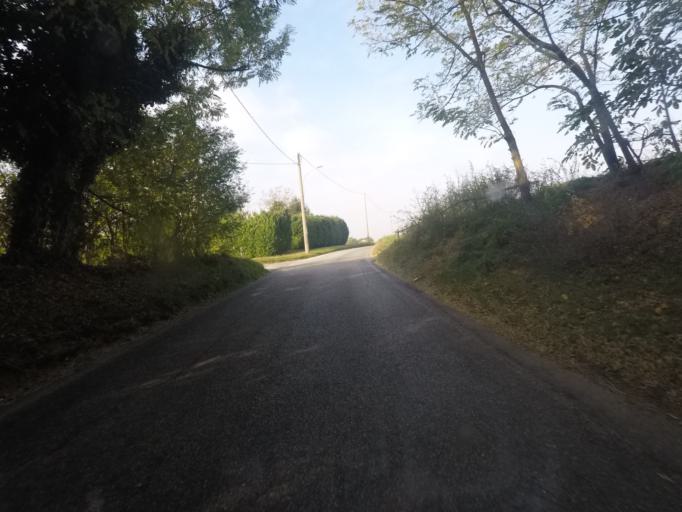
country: IT
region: Lombardy
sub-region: Provincia di Monza e Brianza
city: Bellusco
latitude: 45.6265
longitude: 9.4065
